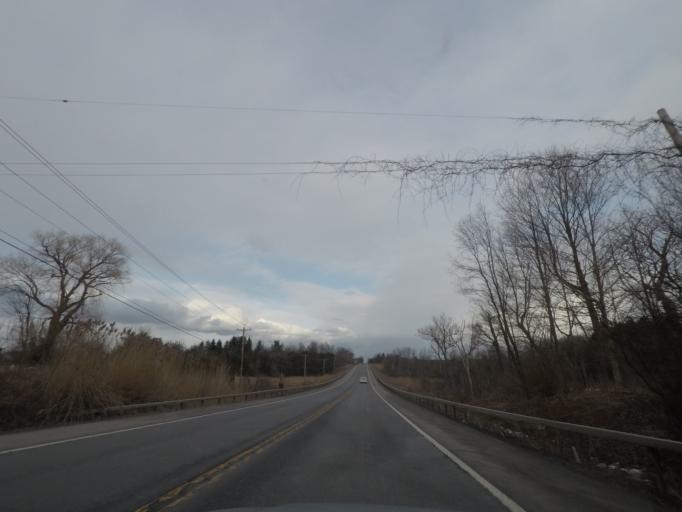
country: US
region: New York
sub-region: Oneida County
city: Vernon
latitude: 43.0725
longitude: -75.4824
